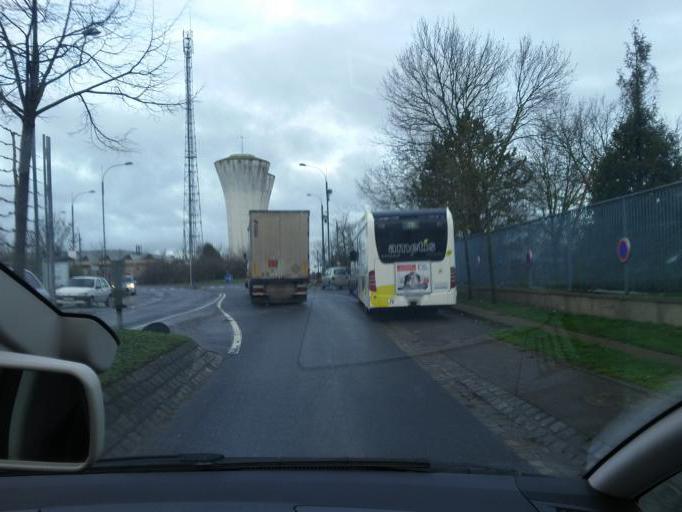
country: FR
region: Picardie
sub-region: Departement de la Somme
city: Poulainville
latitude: 49.9346
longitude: 2.2713
